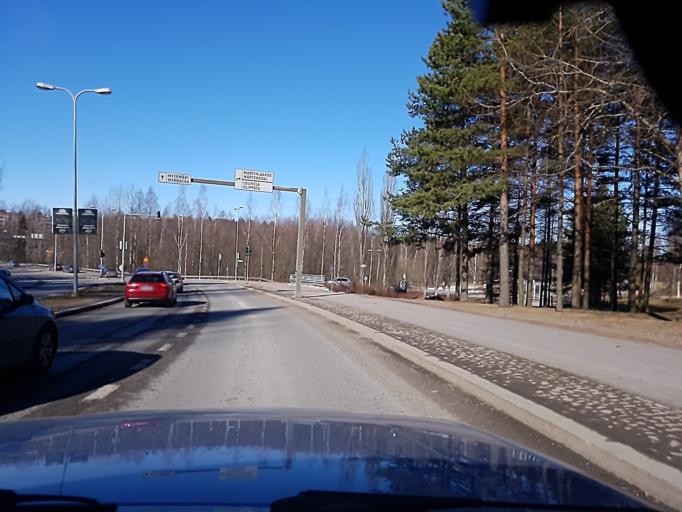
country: FI
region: Uusimaa
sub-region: Helsinki
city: Teekkarikylae
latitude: 60.2637
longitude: 24.8684
